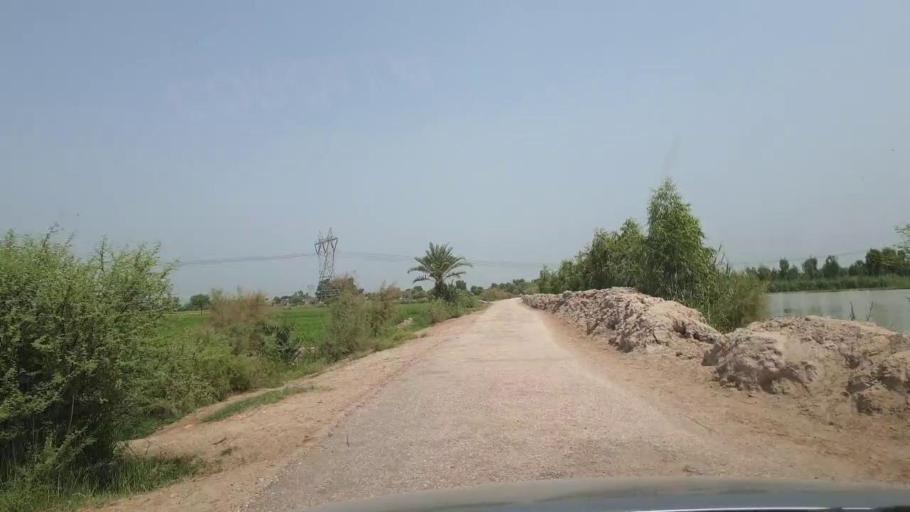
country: PK
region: Sindh
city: Madeji
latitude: 27.8033
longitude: 68.5202
